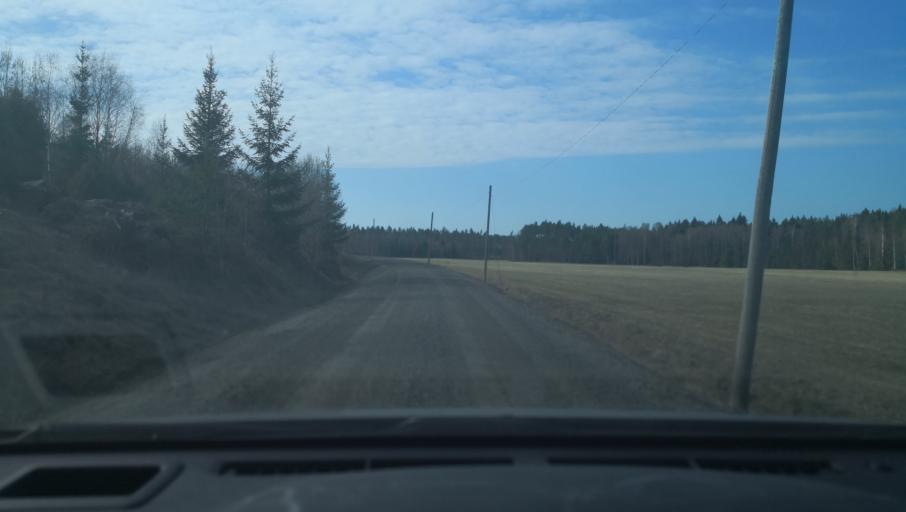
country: SE
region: Uppsala
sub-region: Heby Kommun
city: Heby
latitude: 59.8477
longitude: 16.8917
